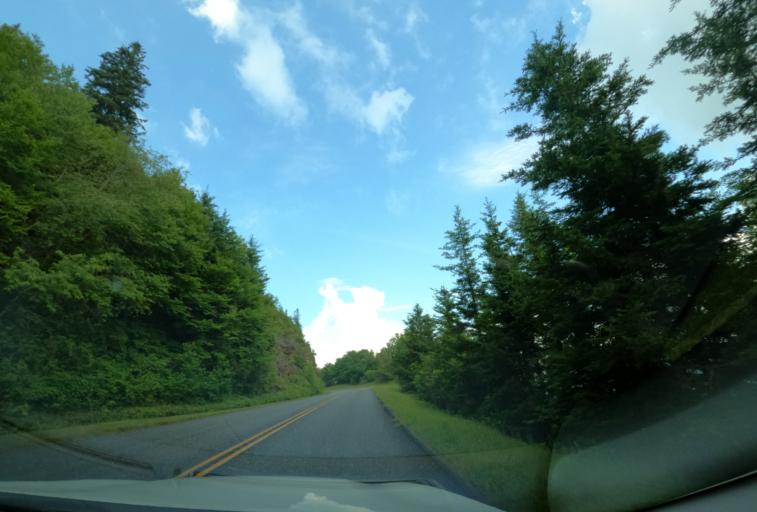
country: US
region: North Carolina
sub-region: Haywood County
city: Hazelwood
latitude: 35.3783
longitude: -83.0082
